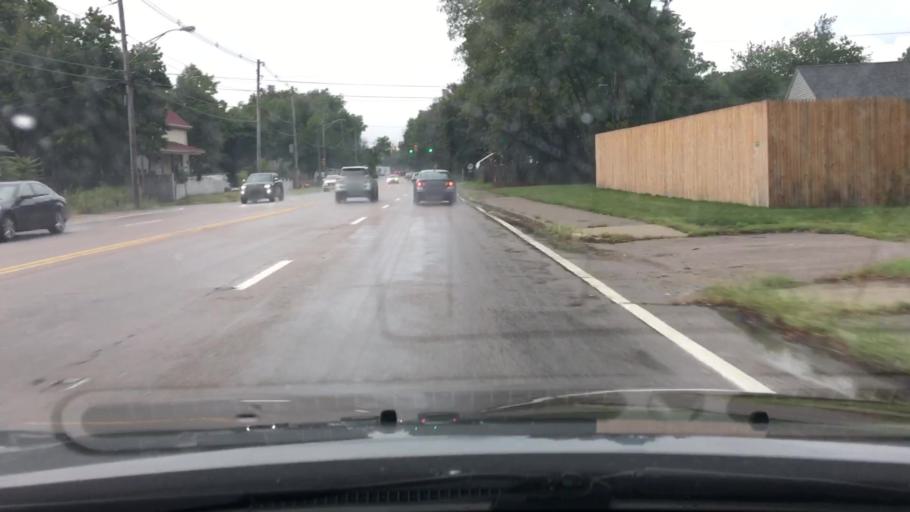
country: US
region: Rhode Island
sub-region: Providence County
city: Valley Falls
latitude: 41.9088
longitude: -71.3576
